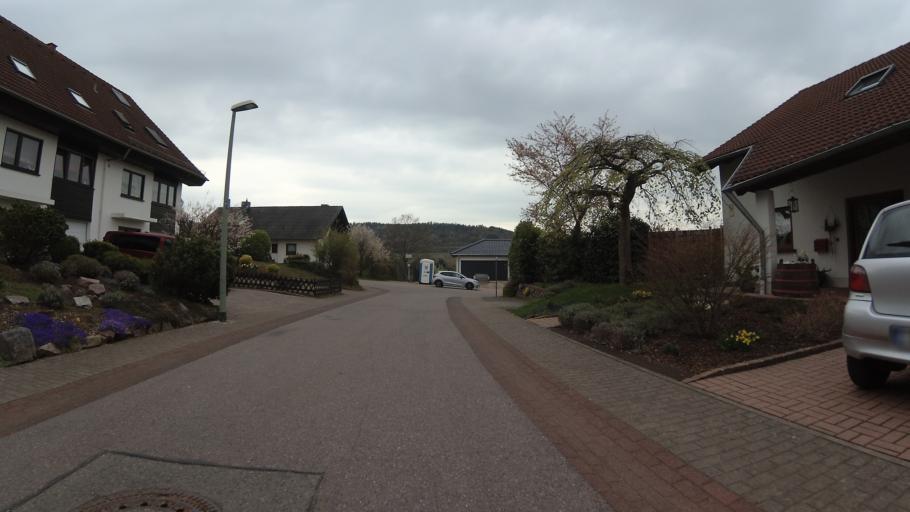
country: DE
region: Saarland
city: Merzig
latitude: 49.4429
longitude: 6.6575
